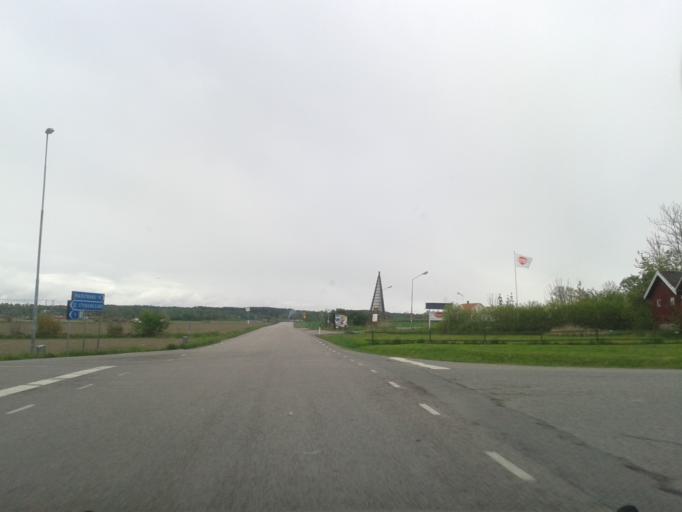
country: SE
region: Vaestra Goetaland
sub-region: Kungalvs Kommun
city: Kode
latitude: 57.9407
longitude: 11.8208
